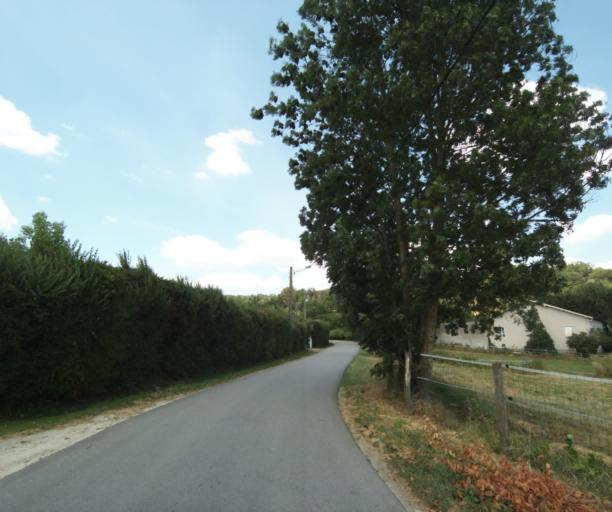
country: FR
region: Lorraine
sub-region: Departement de Meurthe-et-Moselle
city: Luneville
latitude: 48.6001
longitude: 6.4670
